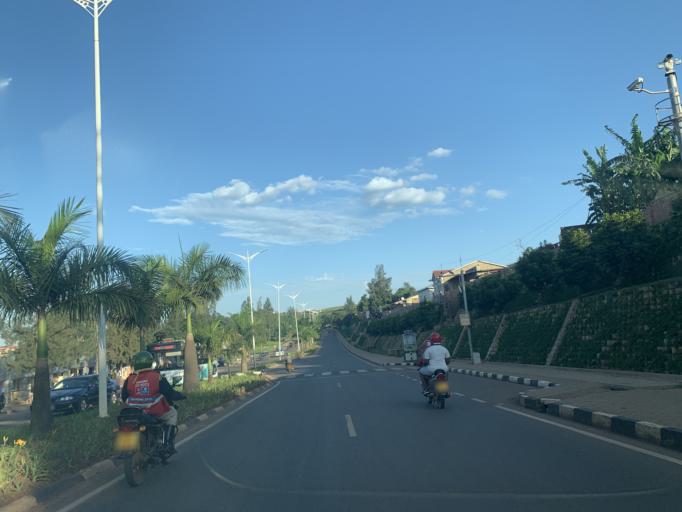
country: RW
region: Kigali
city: Kigali
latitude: -1.9626
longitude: 30.1243
